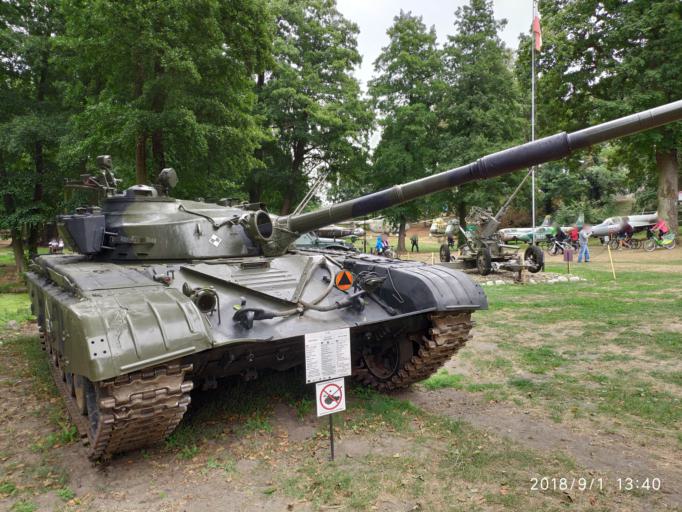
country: PL
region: Lubusz
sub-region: Powiat zielonogorski
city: Swidnica
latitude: 51.9449
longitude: 15.3185
